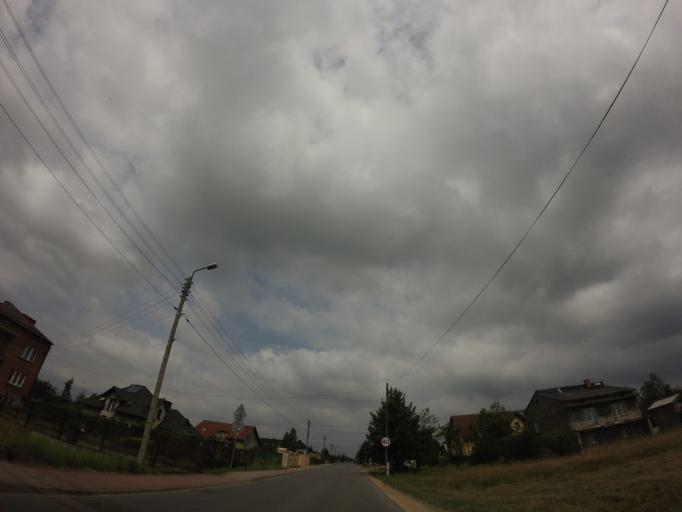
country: PL
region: Lesser Poland Voivodeship
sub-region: Powiat oswiecimski
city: Chelmek
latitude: 50.0790
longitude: 19.2329
